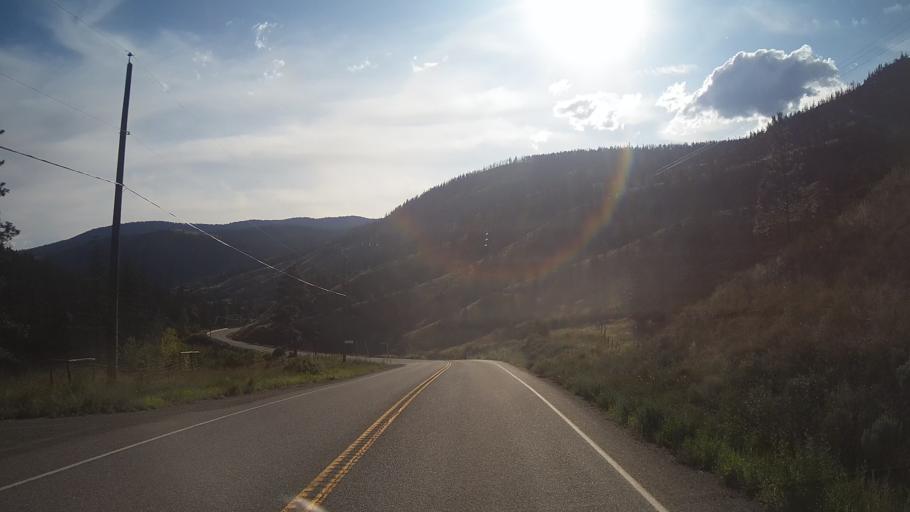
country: CA
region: British Columbia
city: Cache Creek
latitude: 50.8846
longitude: -121.4935
